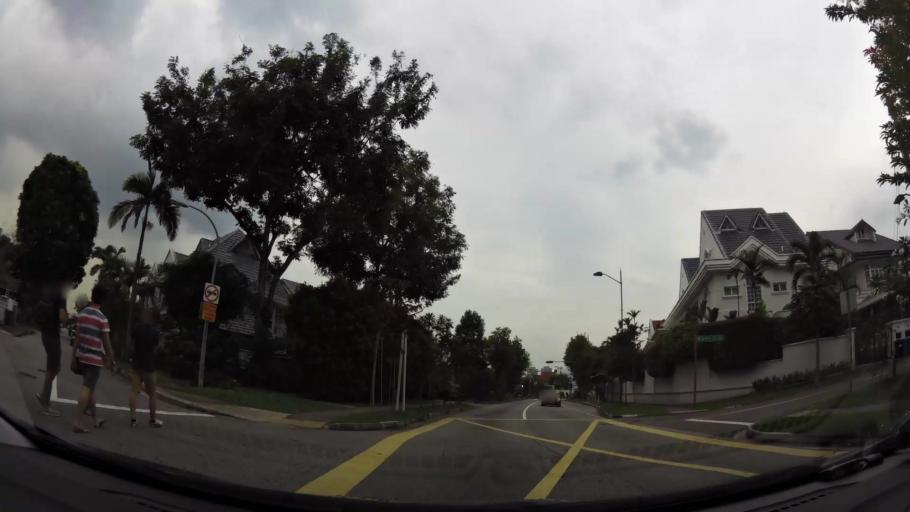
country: SG
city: Singapore
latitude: 1.3633
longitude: 103.8705
